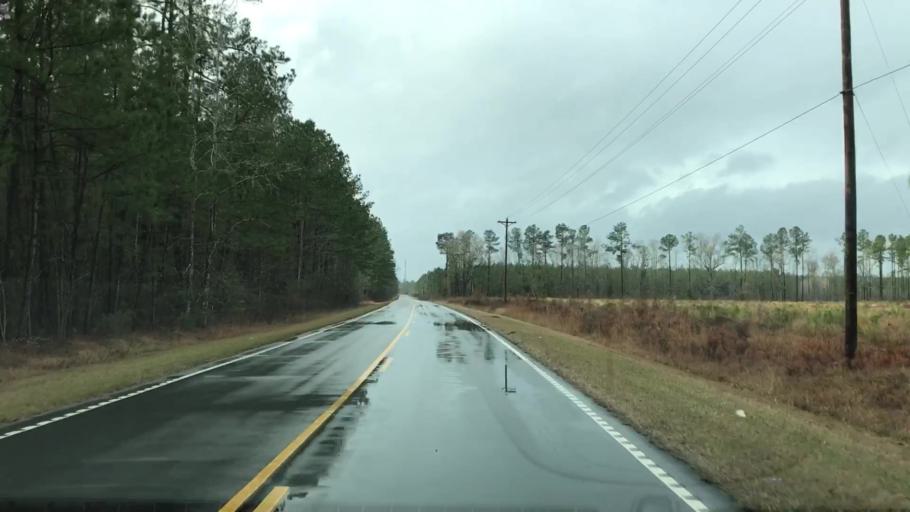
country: US
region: South Carolina
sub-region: Florence County
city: Johnsonville
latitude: 33.6759
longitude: -79.3365
